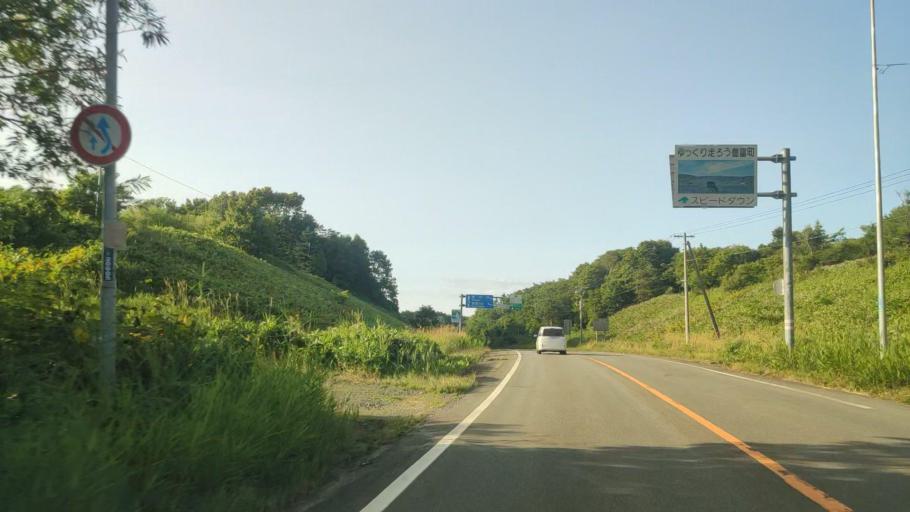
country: JP
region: Hokkaido
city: Makubetsu
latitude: 45.0754
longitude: 141.7540
